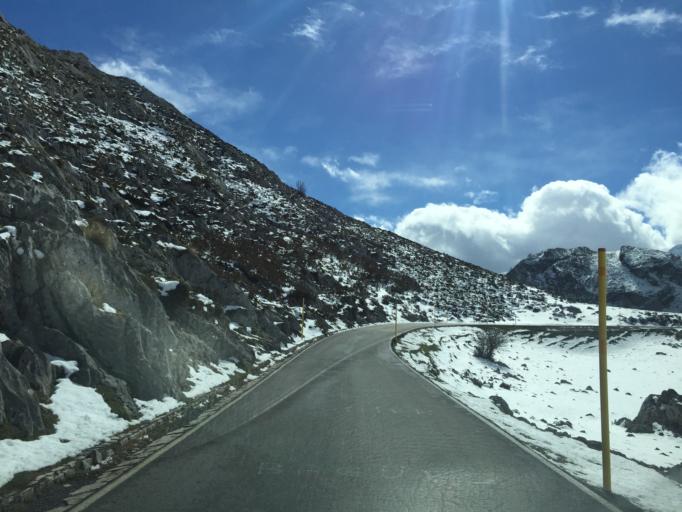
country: ES
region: Asturias
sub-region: Province of Asturias
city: Amieva
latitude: 43.2762
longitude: -4.9960
